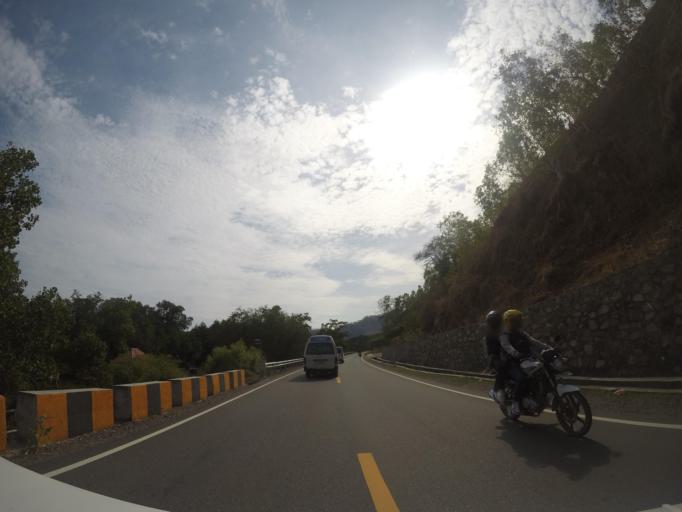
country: ID
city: Metinaro
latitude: -8.5350
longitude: 125.6950
